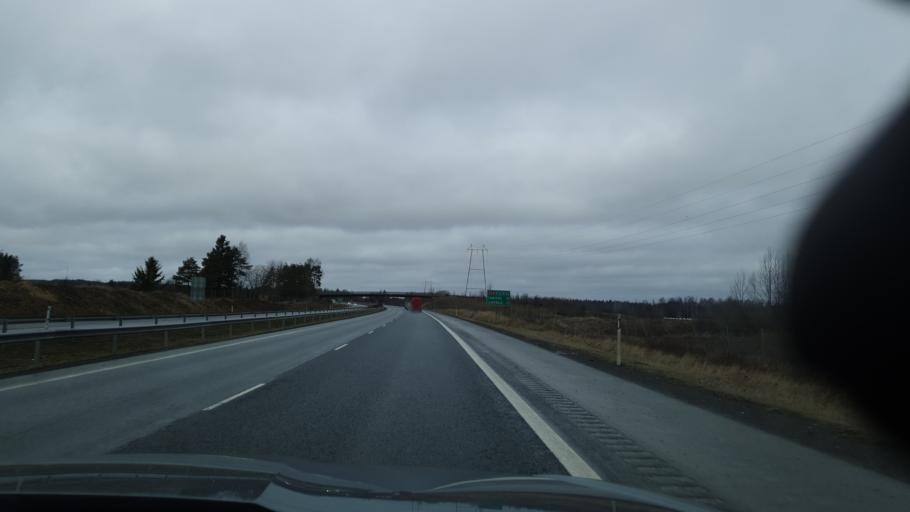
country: FI
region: Pirkanmaa
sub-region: Etelae-Pirkanmaa
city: Akaa
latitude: 61.1893
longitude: 23.8736
